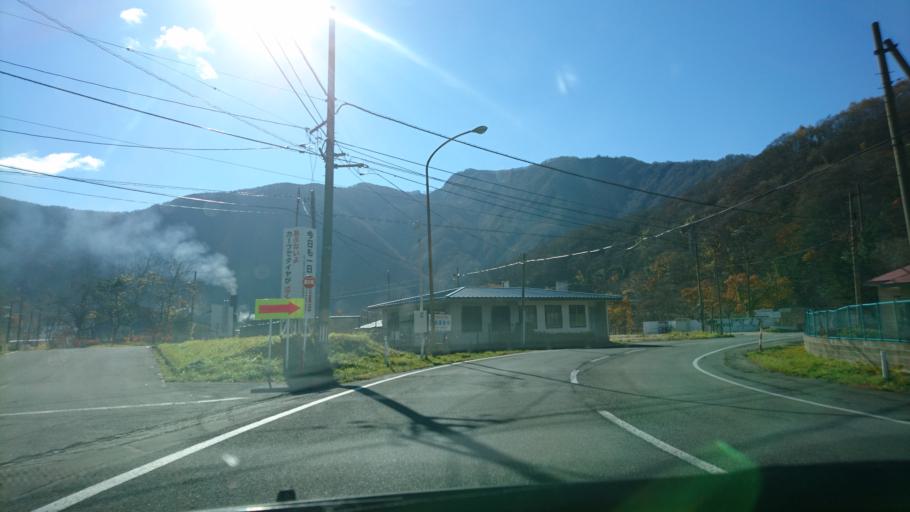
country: JP
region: Iwate
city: Kitakami
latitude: 39.3052
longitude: 140.9024
